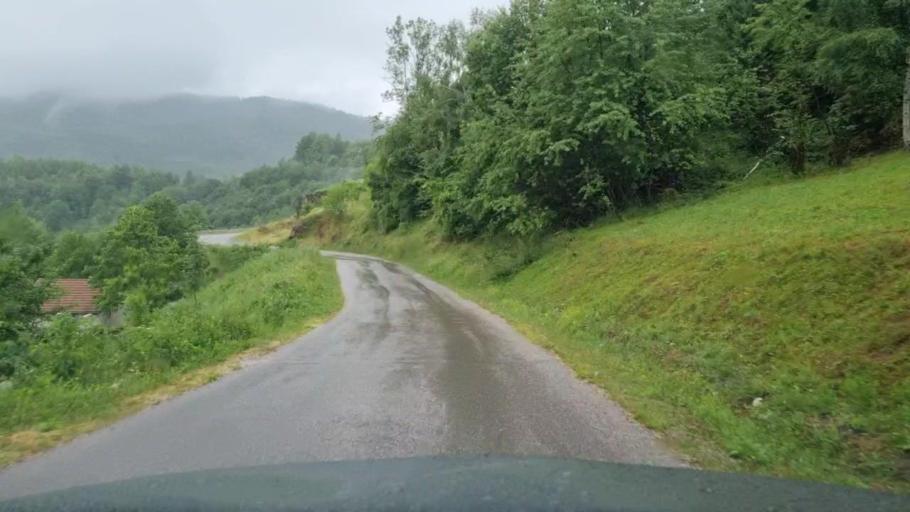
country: BA
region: Federation of Bosnia and Herzegovina
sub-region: Bosansko-Podrinjski Kanton
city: Ustikolina
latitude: 43.6360
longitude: 18.6194
